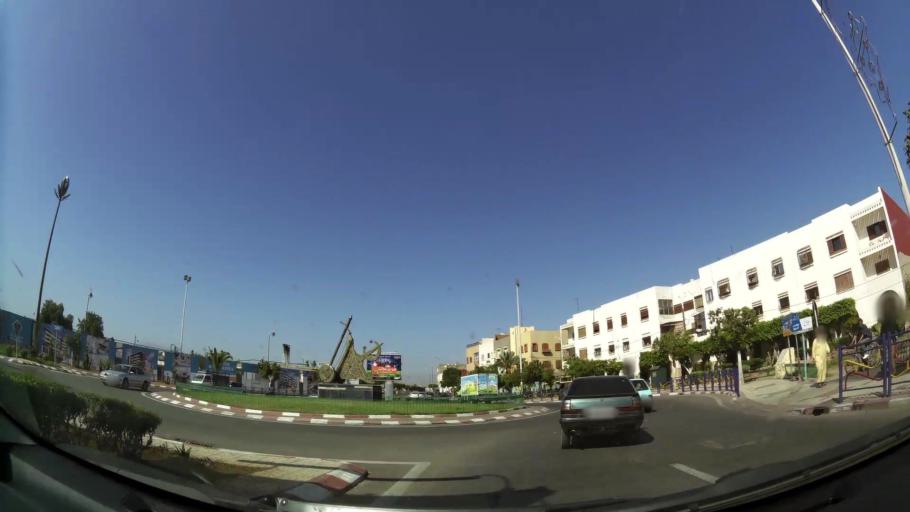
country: MA
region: Souss-Massa-Draa
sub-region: Inezgane-Ait Mellou
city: Inezgane
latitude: 30.3712
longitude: -9.5320
